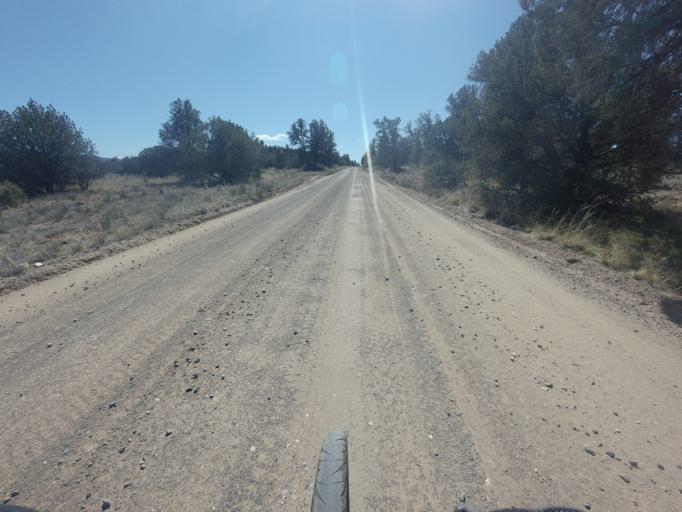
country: US
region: Arizona
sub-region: Yavapai County
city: Lake Montezuma
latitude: 34.6134
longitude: -111.7250
